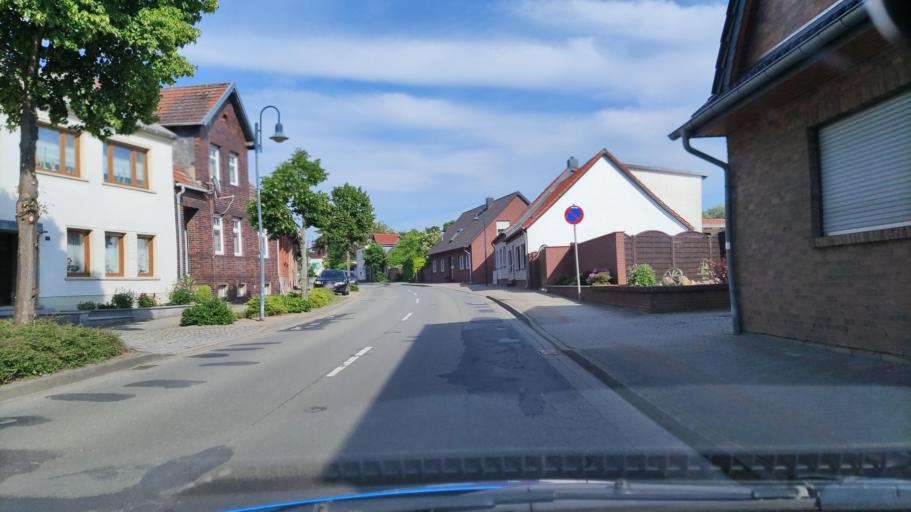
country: DE
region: Saxony-Anhalt
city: Klotze
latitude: 52.6231
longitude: 11.1686
